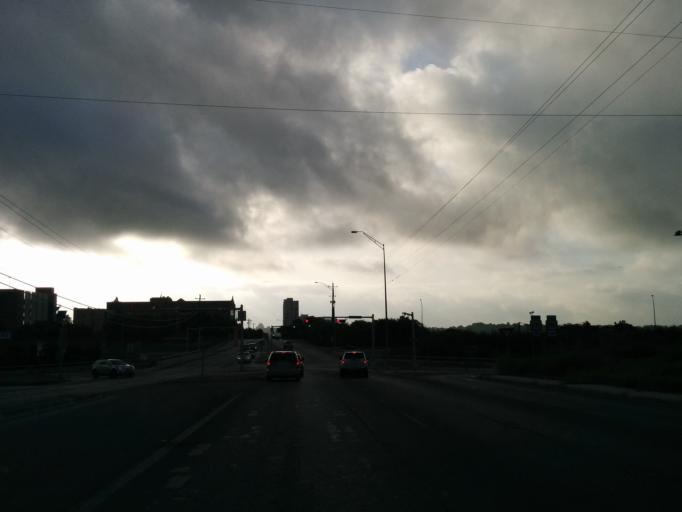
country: US
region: Texas
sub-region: Bexar County
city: Olmos Park
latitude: 29.4655
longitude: -98.4750
